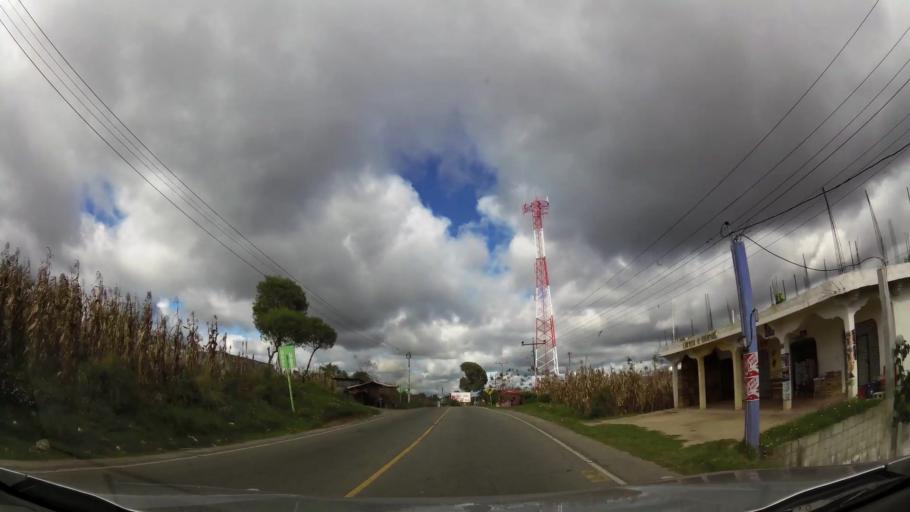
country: GT
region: Quiche
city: Chichicastenango
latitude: 14.8712
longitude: -91.1423
